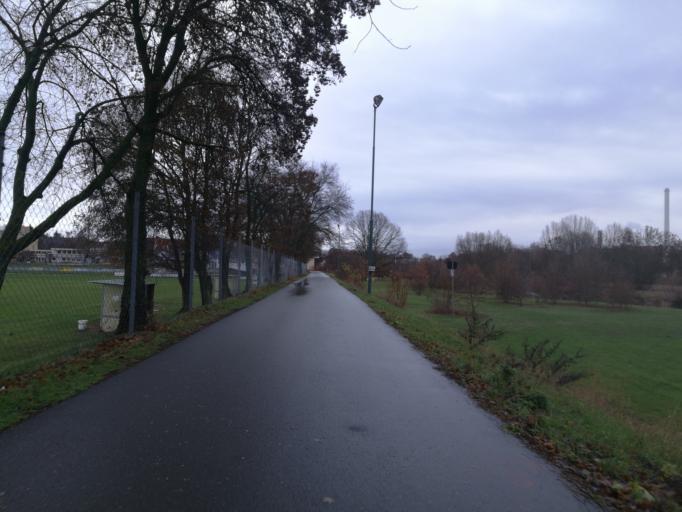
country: DE
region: Bavaria
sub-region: Regierungsbezirk Mittelfranken
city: Wetzendorf
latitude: 49.4675
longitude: 11.0220
